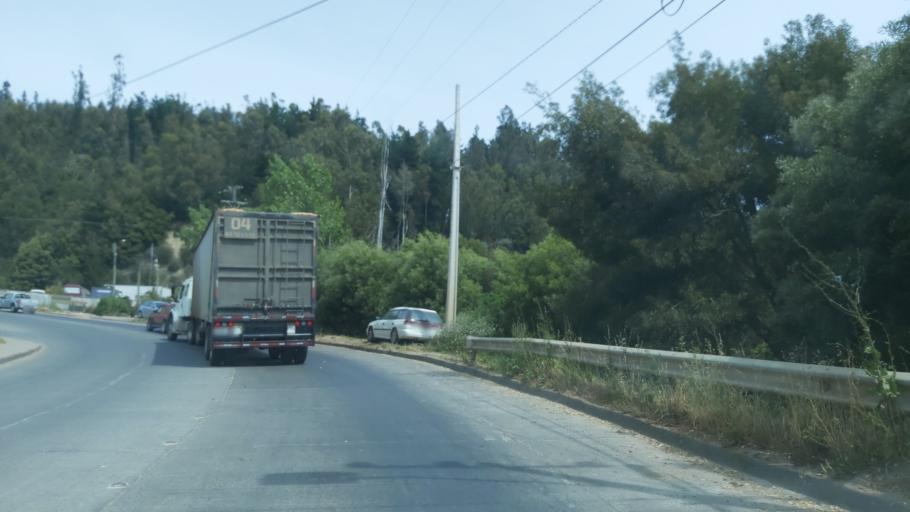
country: CL
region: Maule
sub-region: Provincia de Talca
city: Constitucion
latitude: -35.3456
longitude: -72.4189
